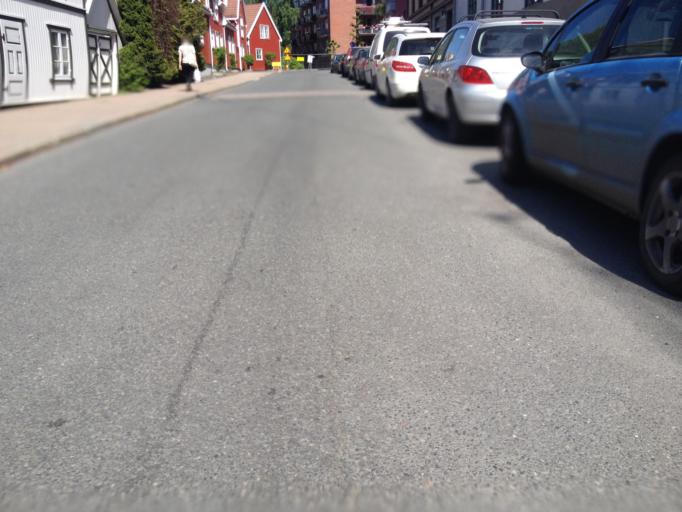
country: NO
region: Oslo
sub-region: Oslo
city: Oslo
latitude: 59.9346
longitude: 10.7624
